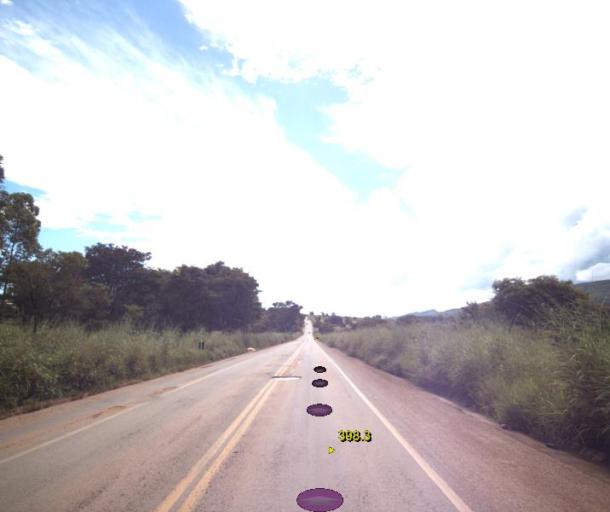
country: BR
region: Goias
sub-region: Pirenopolis
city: Pirenopolis
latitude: -16.0154
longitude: -49.1158
